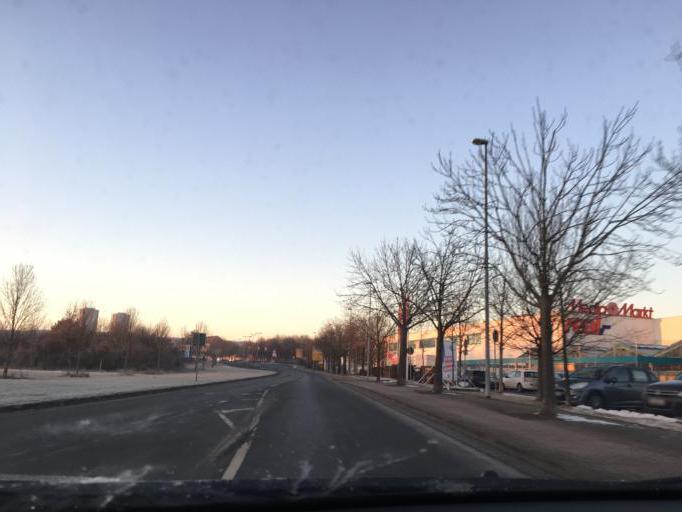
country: DE
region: Thuringia
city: Erfurt
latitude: 50.9713
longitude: 11.0631
